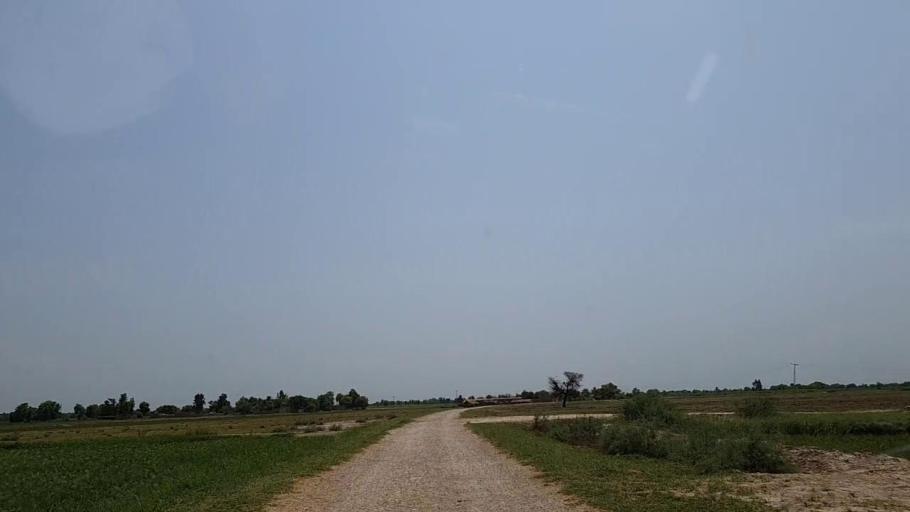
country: PK
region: Sindh
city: Ghotki
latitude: 27.9908
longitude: 69.4098
